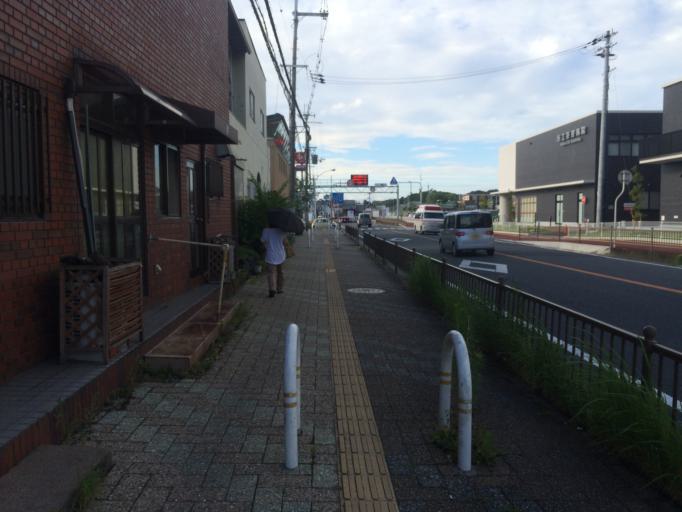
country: JP
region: Nara
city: Nara-shi
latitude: 34.6718
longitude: 135.8347
